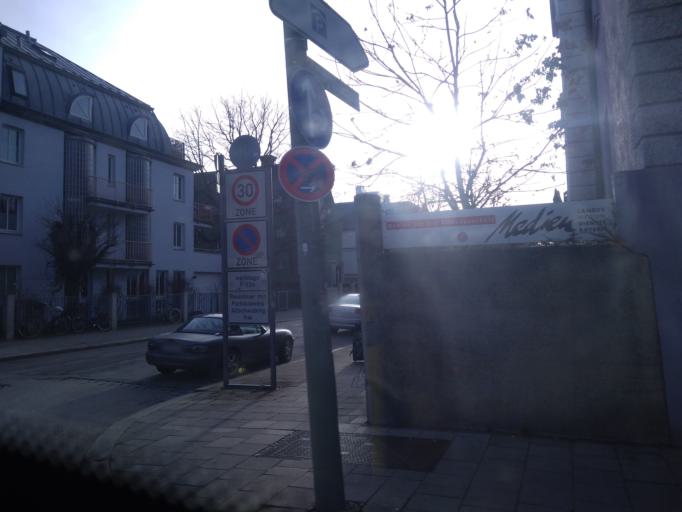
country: DE
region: Bavaria
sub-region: Upper Bavaria
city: Bogenhausen
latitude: 48.1660
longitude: 11.5915
